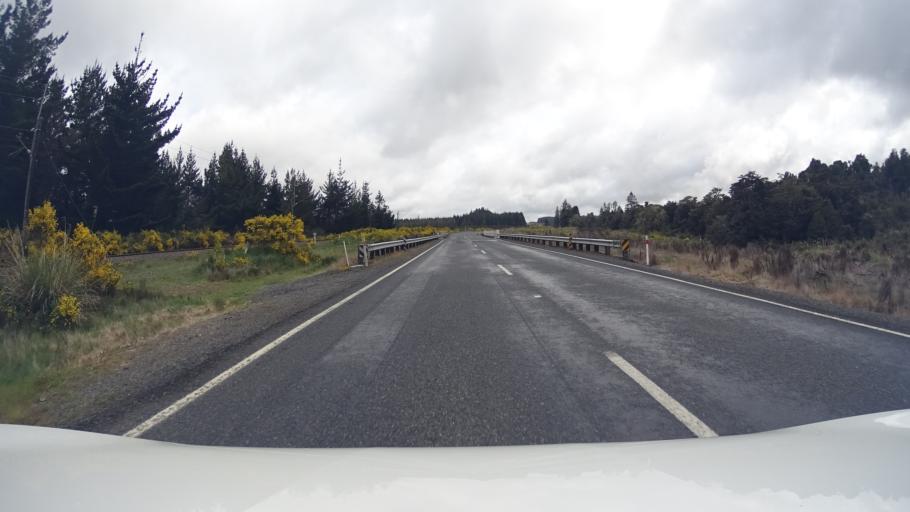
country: NZ
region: Manawatu-Wanganui
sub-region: Ruapehu District
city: Waiouru
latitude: -39.2183
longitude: 175.4005
